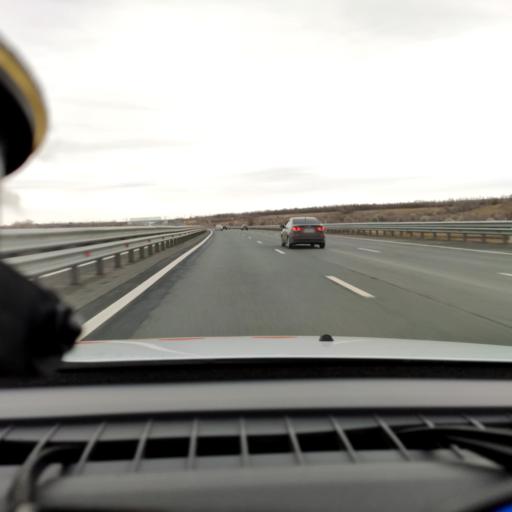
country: RU
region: Samara
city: Smyshlyayevka
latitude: 53.1501
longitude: 50.3628
